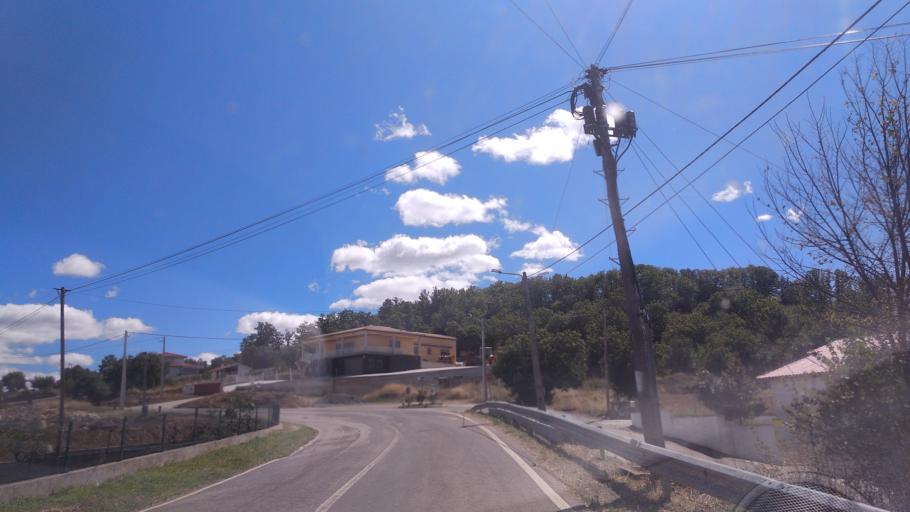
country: PT
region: Braganca
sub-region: Braganca Municipality
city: Braganca
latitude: 41.7830
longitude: -6.7655
